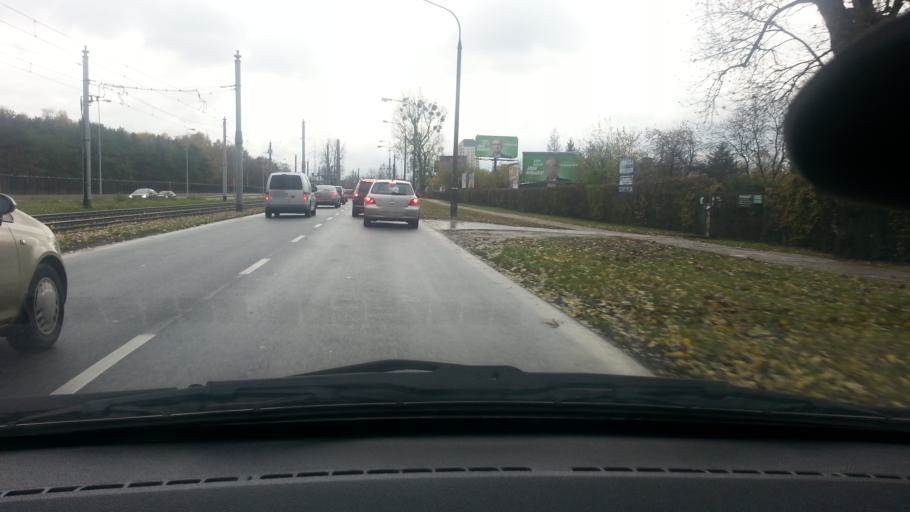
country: PL
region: Masovian Voivodeship
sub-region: Warszawa
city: Praga Polnoc
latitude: 52.2720
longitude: 21.0334
